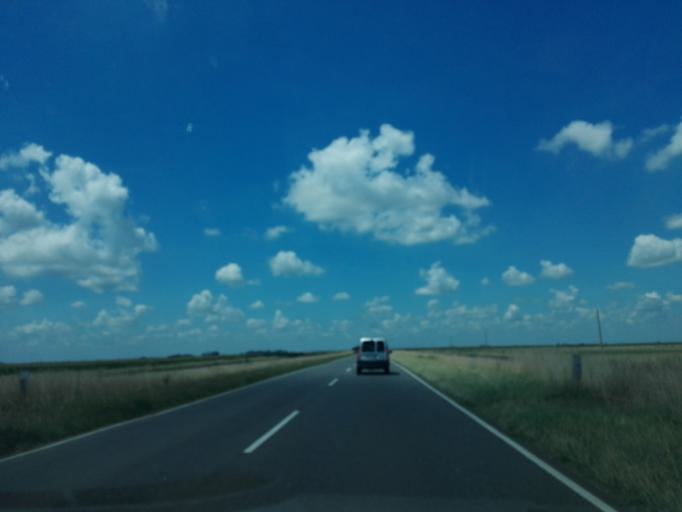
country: AR
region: Buenos Aires
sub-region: Partido de General Belgrano
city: General Belgrano
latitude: -35.8996
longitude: -58.6189
